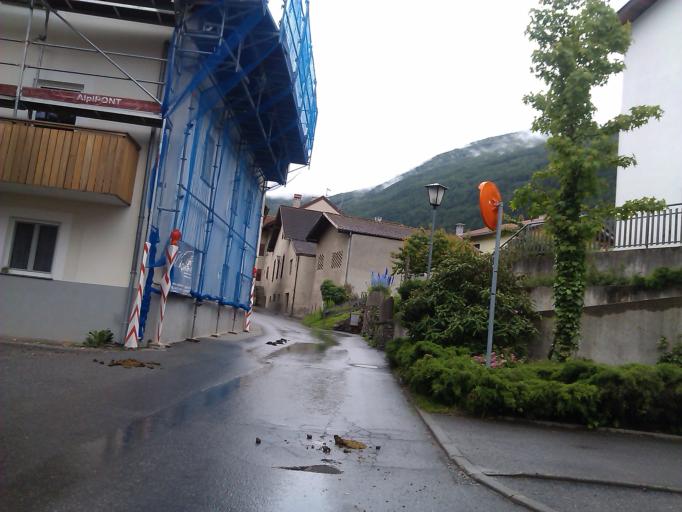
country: IT
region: Trentino-Alto Adige
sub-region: Bolzano
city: Lasa
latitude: 46.6152
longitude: 10.7008
